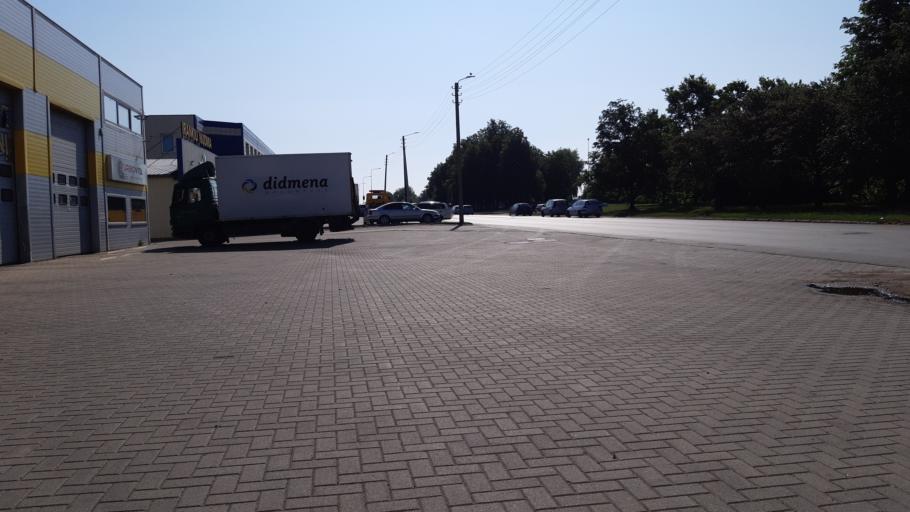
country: LT
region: Kauno apskritis
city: Dainava (Kaunas)
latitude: 54.9136
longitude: 23.9928
